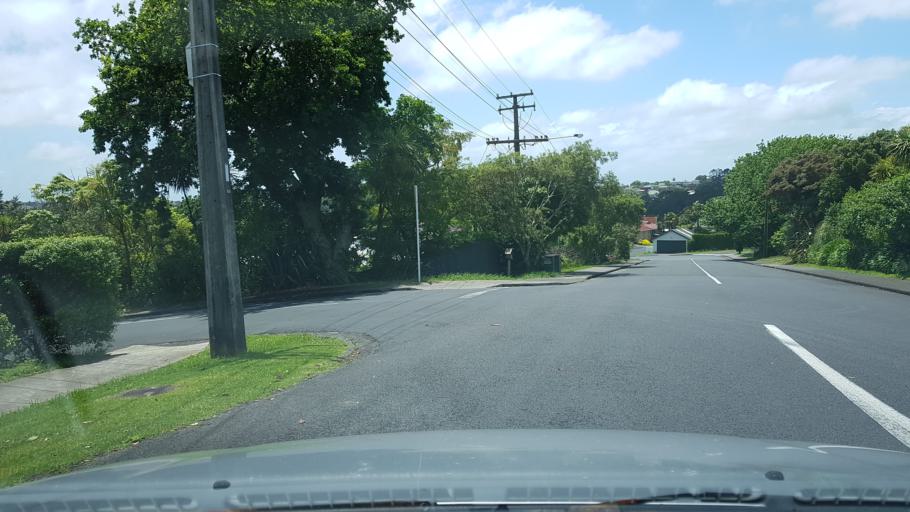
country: NZ
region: Auckland
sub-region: Auckland
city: North Shore
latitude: -36.8080
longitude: 174.7148
